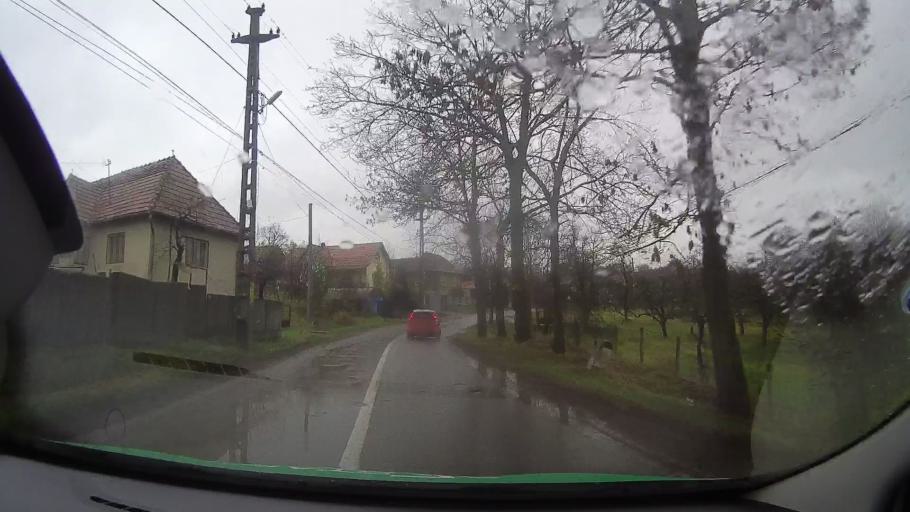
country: RO
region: Mures
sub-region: Comuna Vatava
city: Vatava
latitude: 46.9458
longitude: 24.7625
